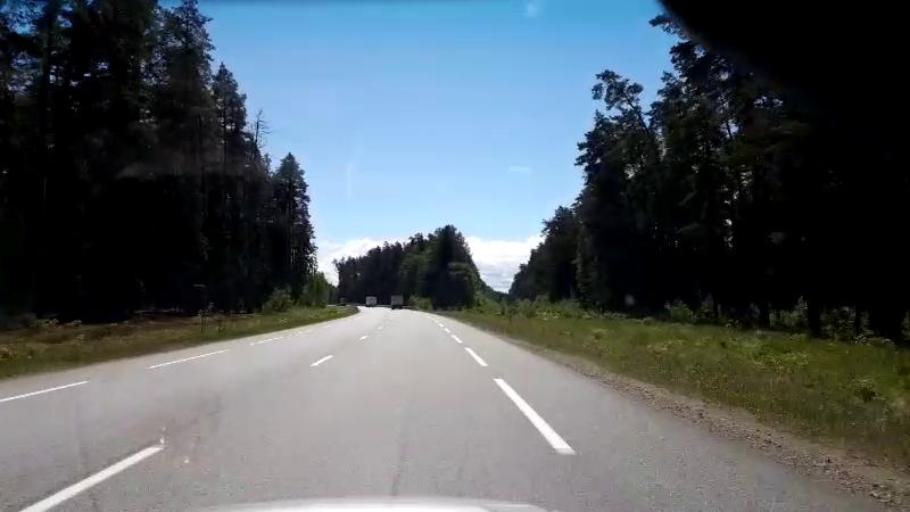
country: LV
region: Saulkrastu
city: Saulkrasti
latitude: 57.3454
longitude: 24.4415
